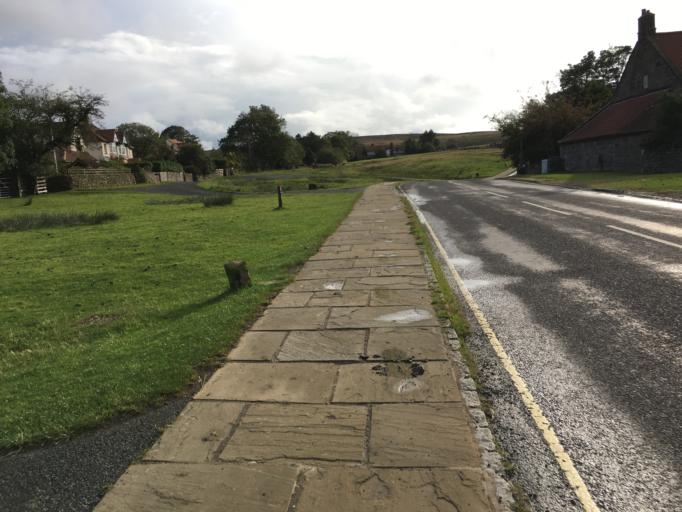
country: GB
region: England
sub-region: North Yorkshire
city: Sleights
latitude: 54.3977
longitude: -0.7226
